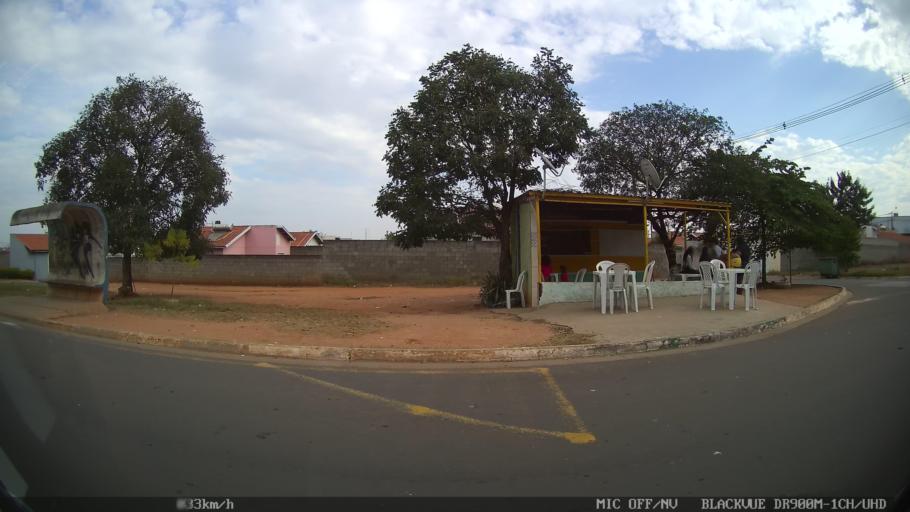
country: BR
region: Sao Paulo
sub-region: Paulinia
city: Paulinia
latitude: -22.7377
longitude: -47.1709
